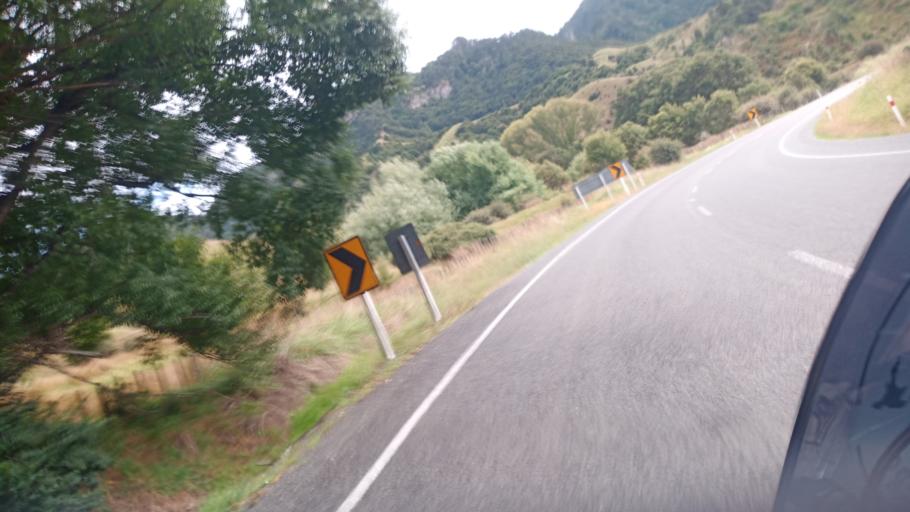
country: NZ
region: Gisborne
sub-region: Gisborne District
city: Gisborne
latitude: -38.2272
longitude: 178.2542
